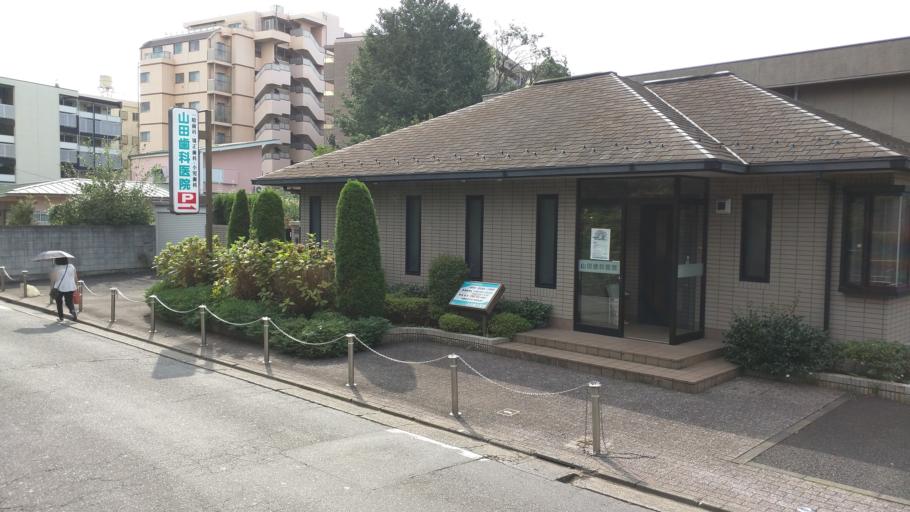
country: JP
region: Tokyo
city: Chofugaoka
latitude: 35.6780
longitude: 139.5137
